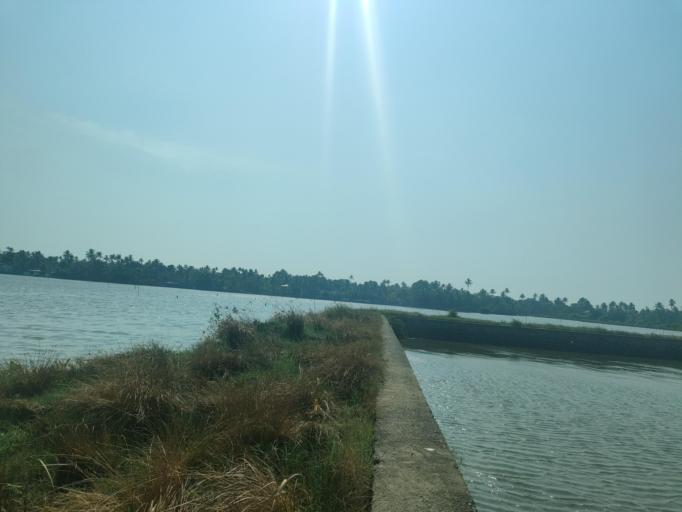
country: IN
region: Kerala
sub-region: Ernakulam
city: Elur
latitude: 10.0751
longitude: 76.2262
